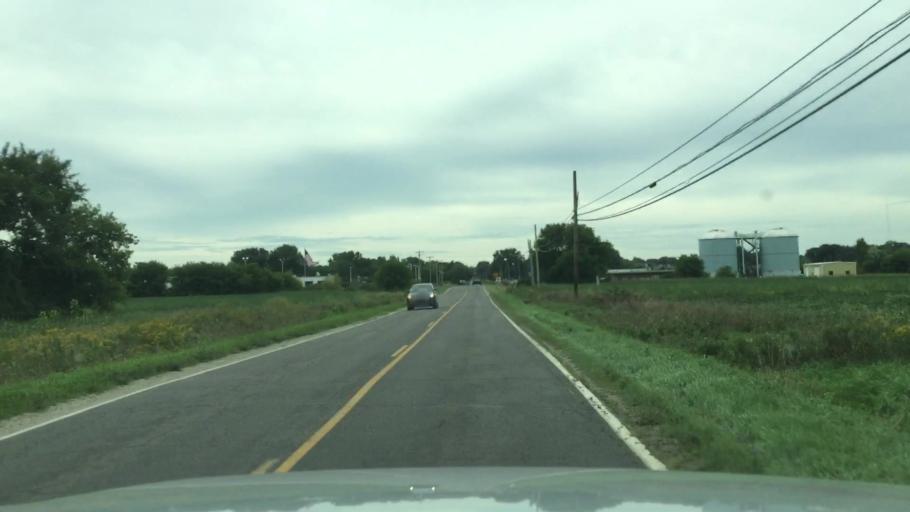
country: US
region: Michigan
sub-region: Shiawassee County
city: Durand
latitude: 42.9294
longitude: -83.9884
